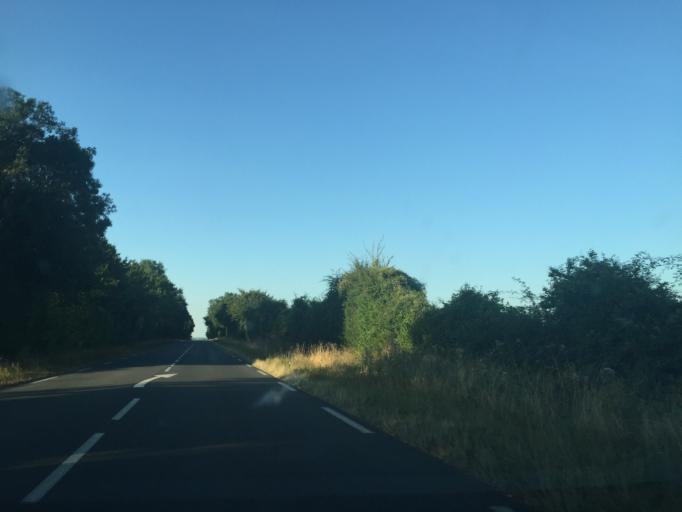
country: FR
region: Poitou-Charentes
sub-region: Departement des Deux-Sevres
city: Lezay
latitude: 46.2909
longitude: -0.0679
